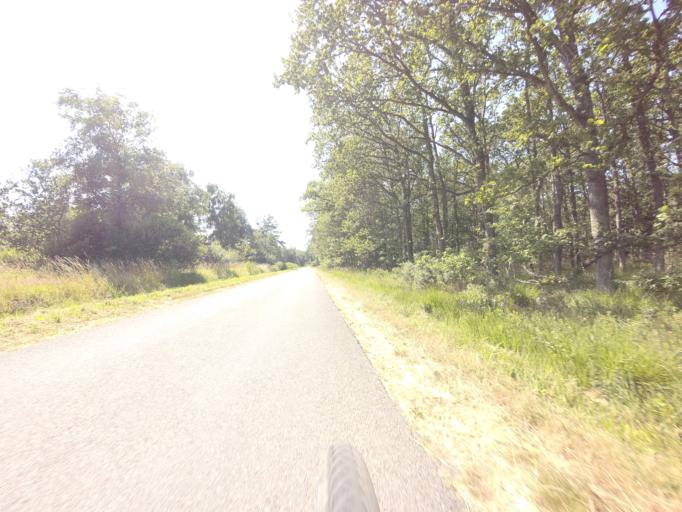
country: DK
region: North Denmark
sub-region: Laeso Kommune
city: Byrum
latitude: 57.2894
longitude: 10.9794
